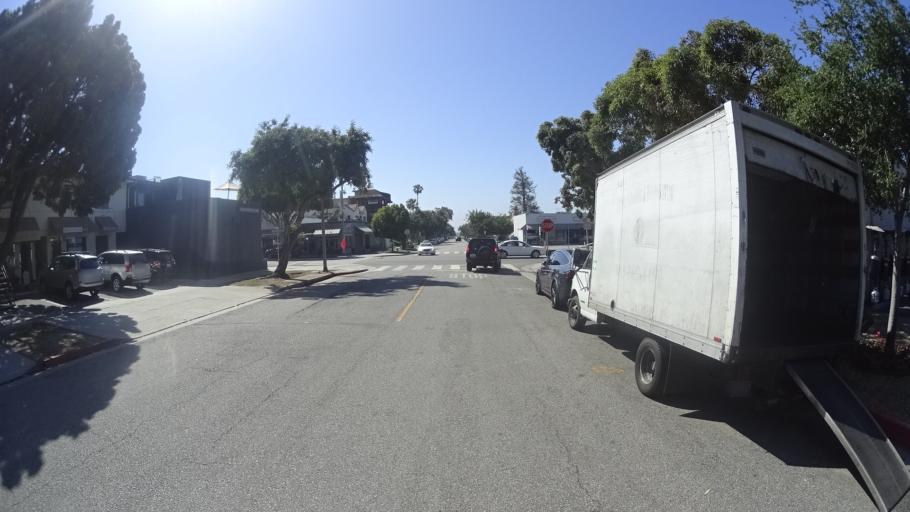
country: US
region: California
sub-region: Los Angeles County
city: Santa Monica
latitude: 34.0294
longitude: -118.4994
